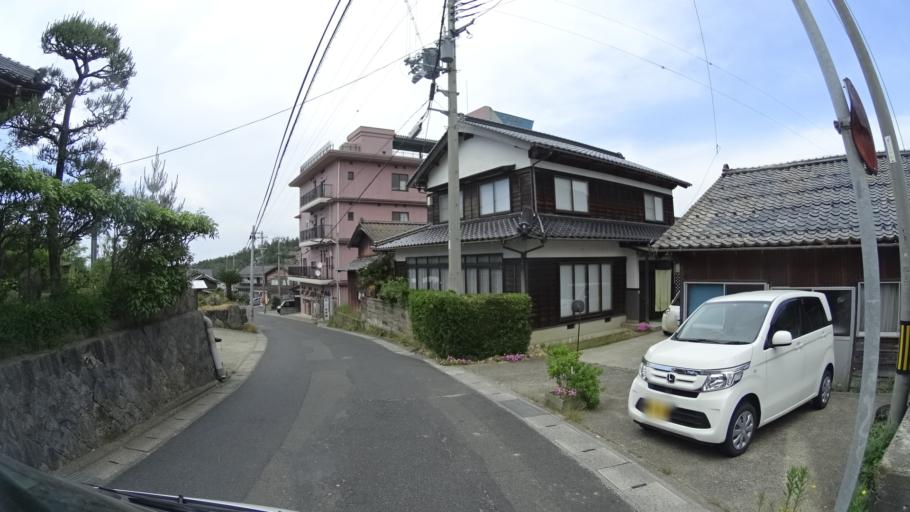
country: JP
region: Kyoto
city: Miyazu
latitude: 35.6977
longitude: 135.0548
